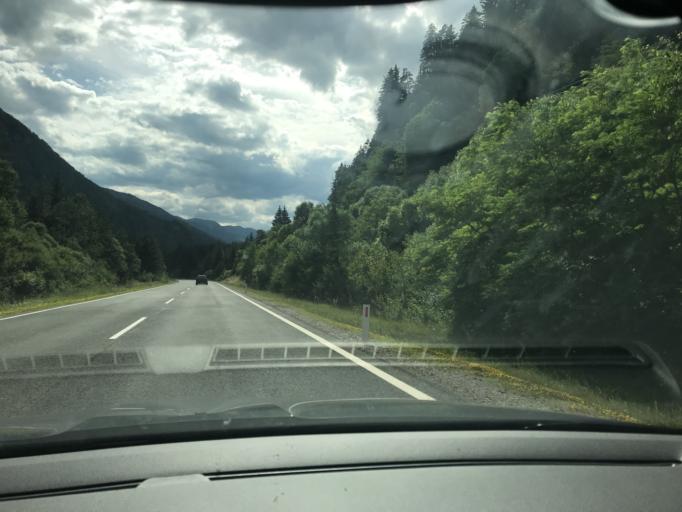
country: AT
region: Tyrol
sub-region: Politischer Bezirk Lienz
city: Anras
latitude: 46.7659
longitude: 12.5713
